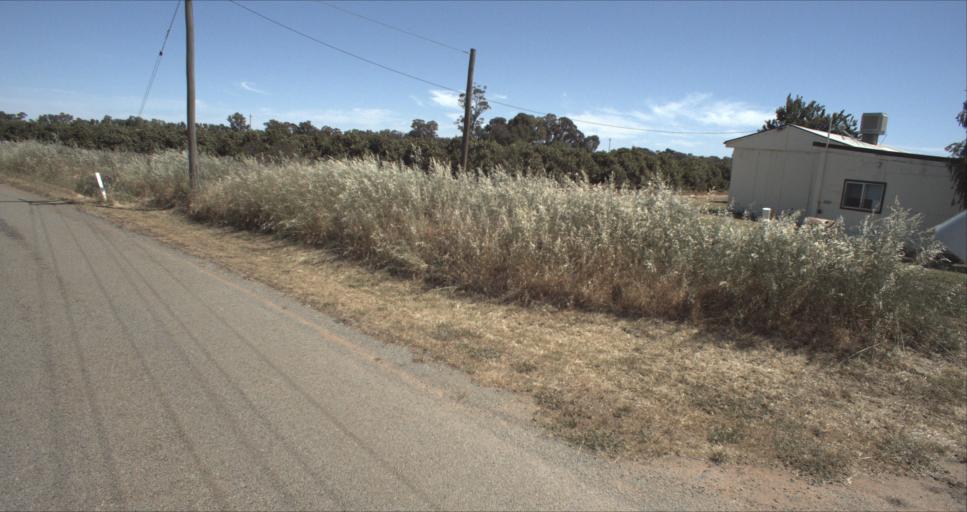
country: AU
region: New South Wales
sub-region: Leeton
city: Leeton
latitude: -34.5275
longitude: 146.3459
